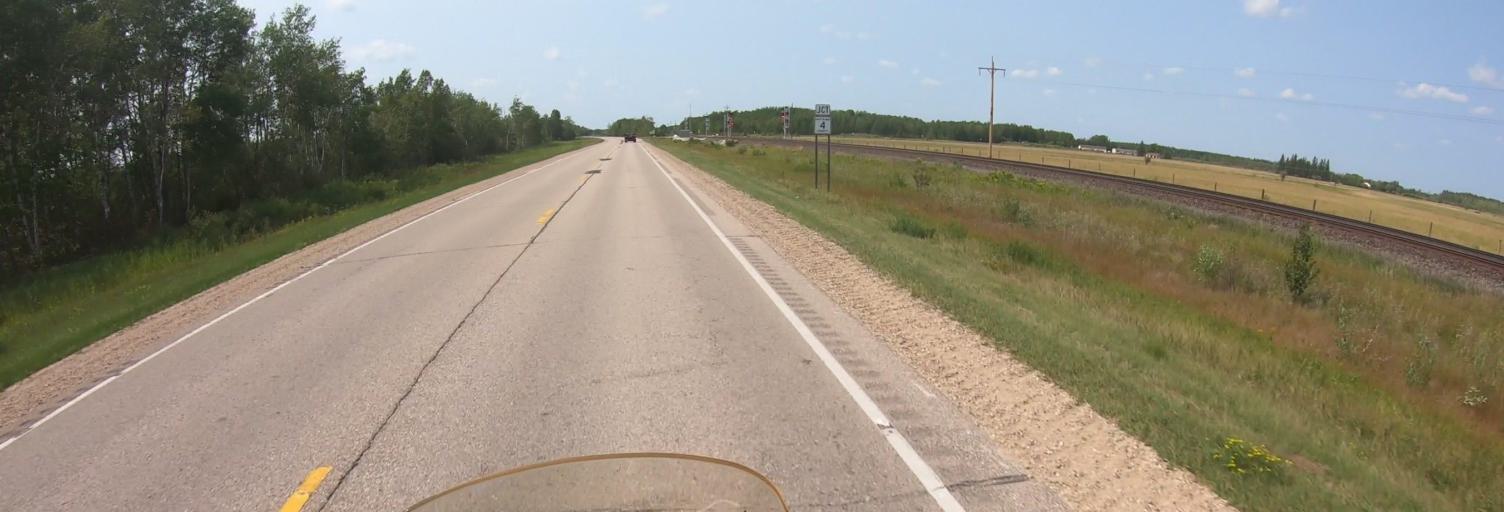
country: US
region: Minnesota
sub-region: Lake of the Woods County
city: Baudette
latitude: 48.7368
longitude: -94.8226
